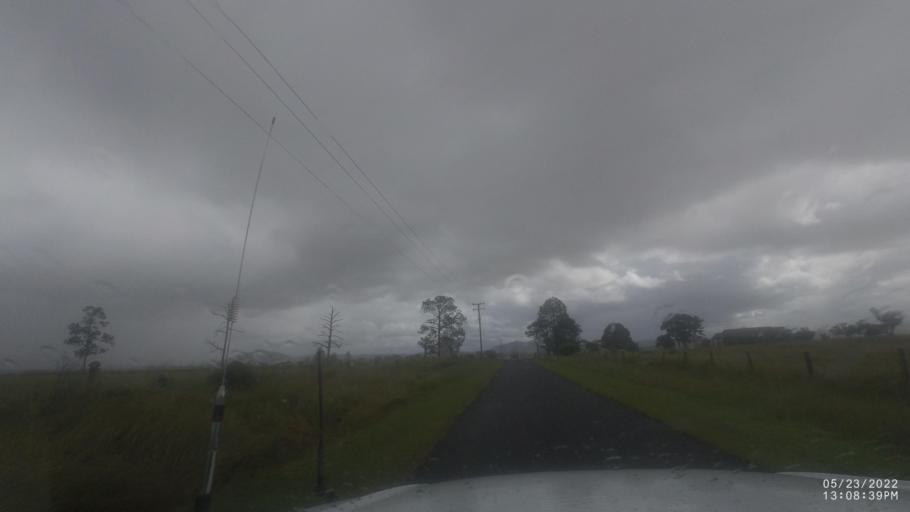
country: AU
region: Queensland
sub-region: Logan
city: Cedar Vale
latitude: -27.9235
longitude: 152.9771
